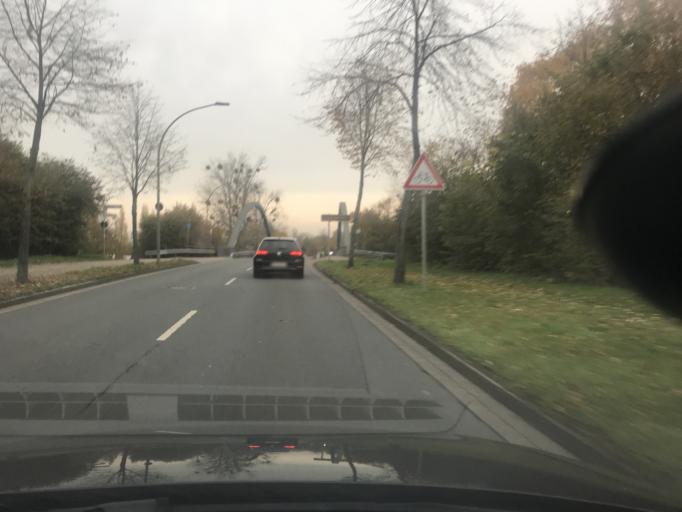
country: DE
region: North Rhine-Westphalia
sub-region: Regierungsbezirk Arnsberg
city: Hamm
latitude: 51.6934
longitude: 7.8826
